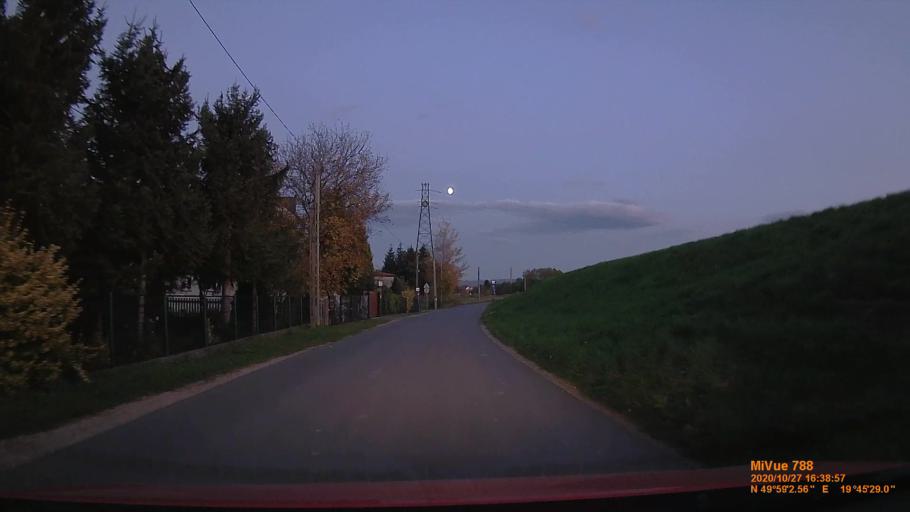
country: PL
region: Lesser Poland Voivodeship
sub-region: Powiat krakowski
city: Raczna
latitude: 49.9840
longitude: 19.7581
